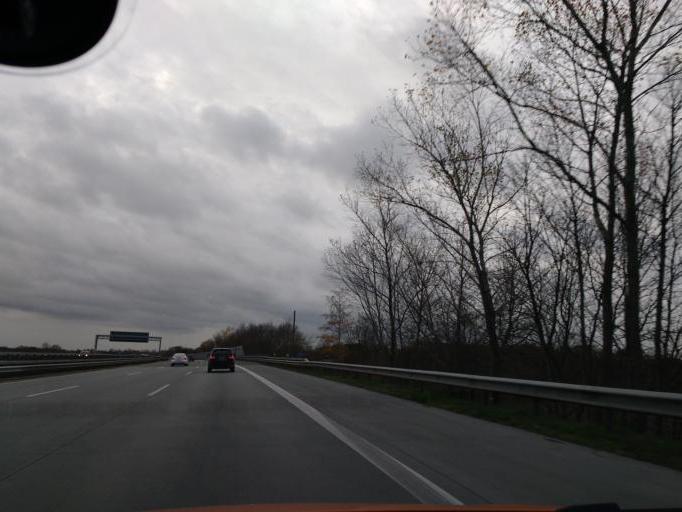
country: DE
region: Lower Saxony
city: Elsdorf
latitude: 53.2301
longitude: 9.3369
